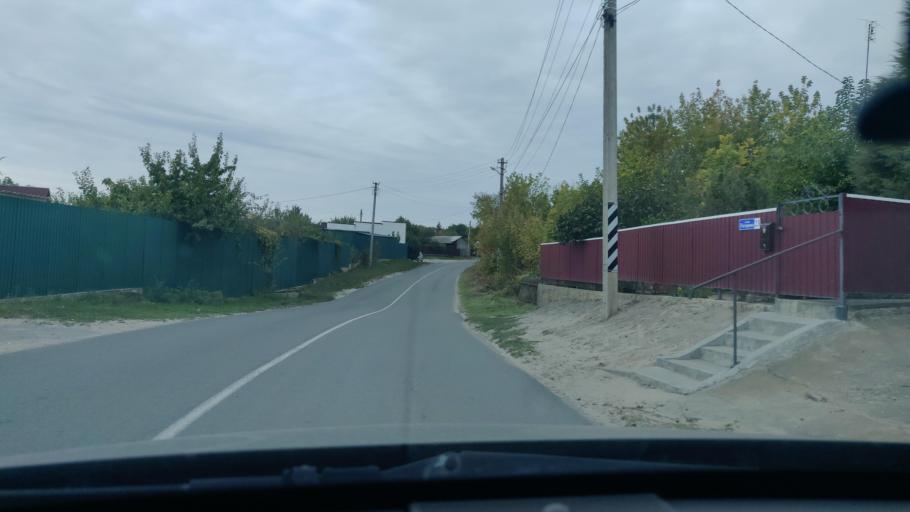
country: RU
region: Rostov
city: Ust'-Donetskiy
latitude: 47.6572
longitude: 40.9114
